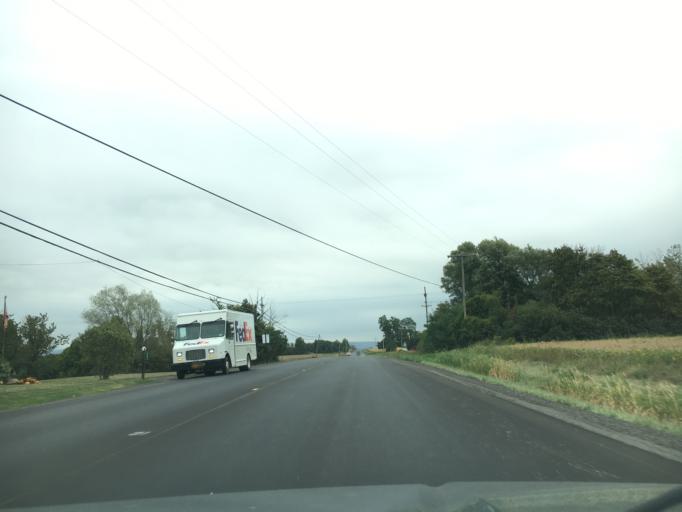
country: US
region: New York
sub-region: Cayuga County
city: Union Springs
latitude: 42.6809
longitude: -76.8138
